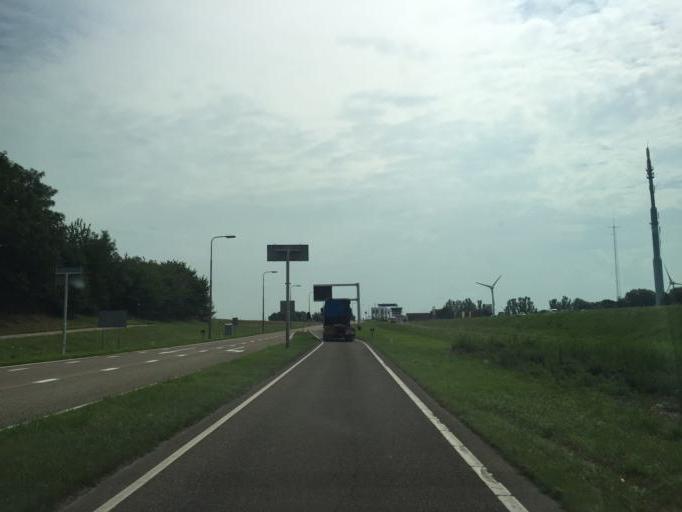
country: NL
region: North Holland
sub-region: Gemeente Enkhuizen
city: Enkhuizen
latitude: 52.6951
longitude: 5.2774
